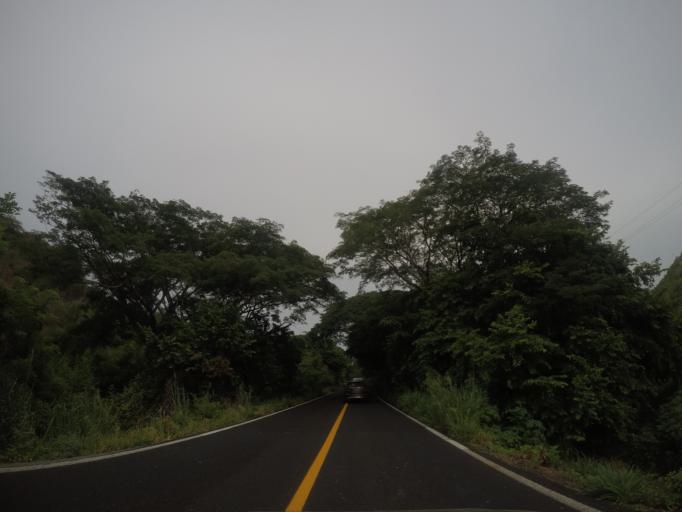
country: MX
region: Oaxaca
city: San Pedro Mixtepec
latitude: 15.9510
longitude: -97.2727
